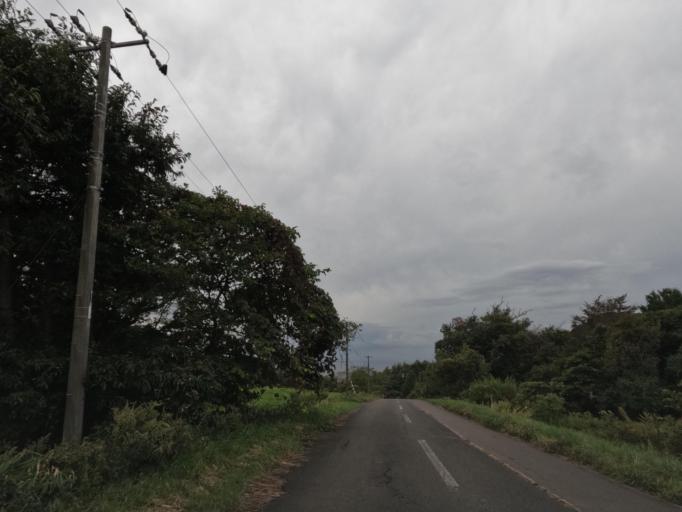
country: JP
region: Hokkaido
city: Date
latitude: 42.4055
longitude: 140.9182
